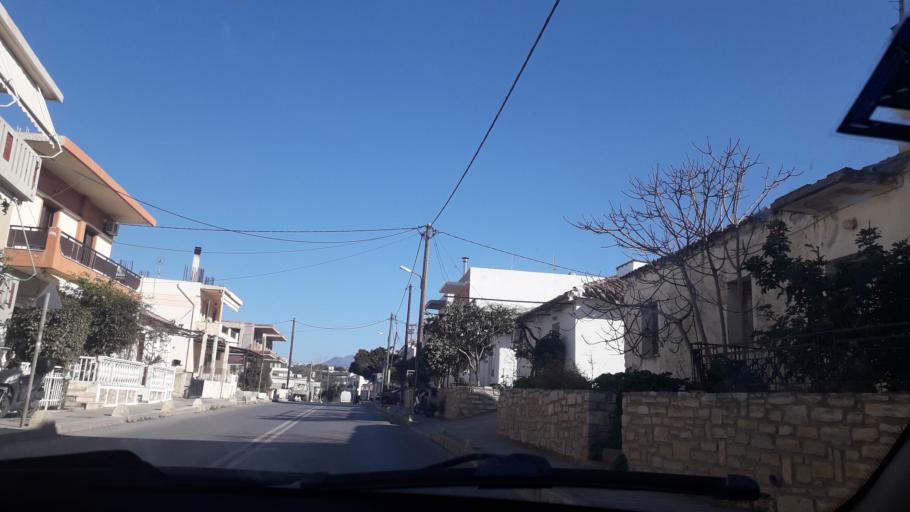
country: GR
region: Crete
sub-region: Nomos Rethymnis
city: Rethymno
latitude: 35.3672
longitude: 24.5336
